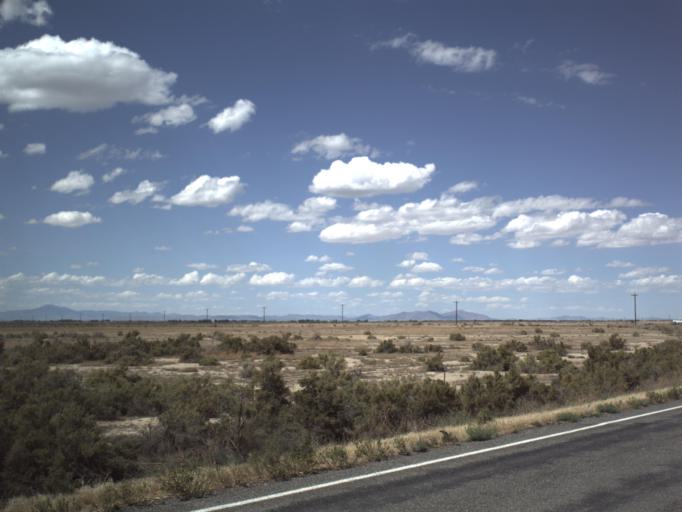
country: US
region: Utah
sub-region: Millard County
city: Delta
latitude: 39.2847
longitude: -112.4625
